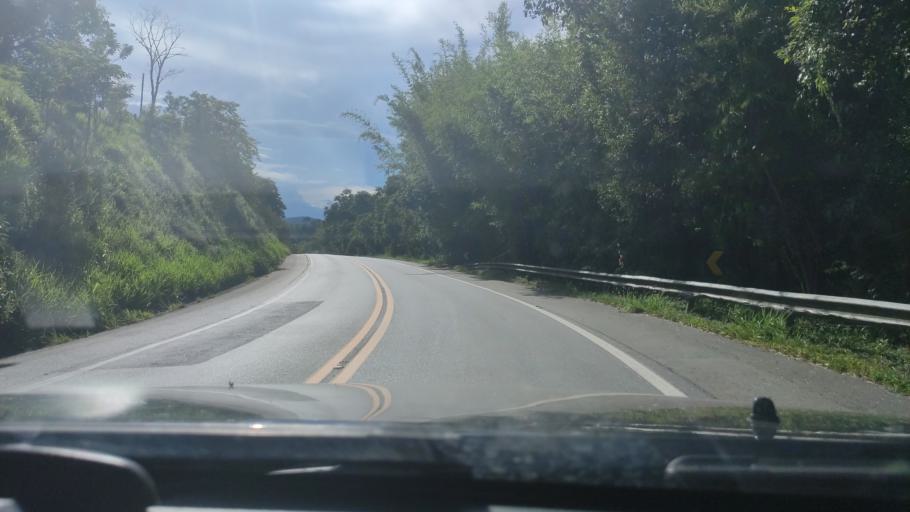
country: BR
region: Sao Paulo
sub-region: Aguas De Lindoia
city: Aguas de Lindoia
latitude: -22.5365
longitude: -46.6291
